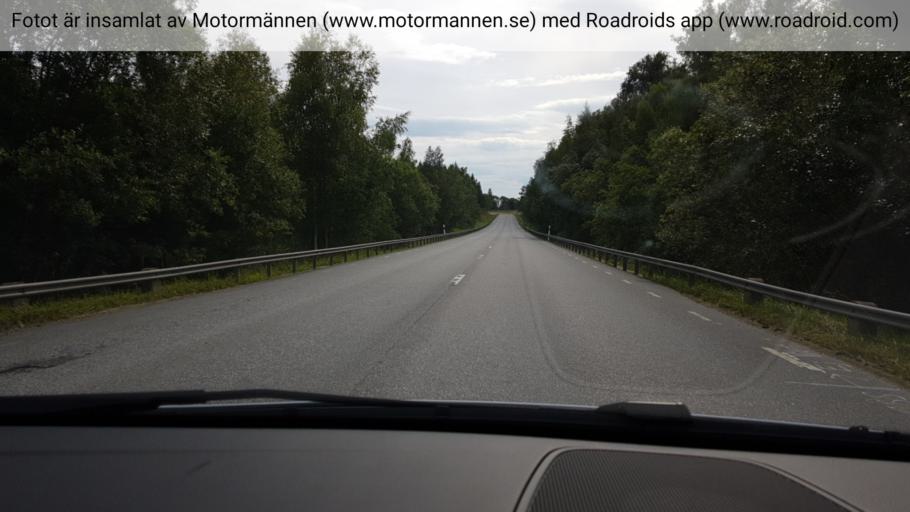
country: SE
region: Uppsala
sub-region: Osthammars Kommun
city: OEsthammar
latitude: 60.2257
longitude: 18.3662
